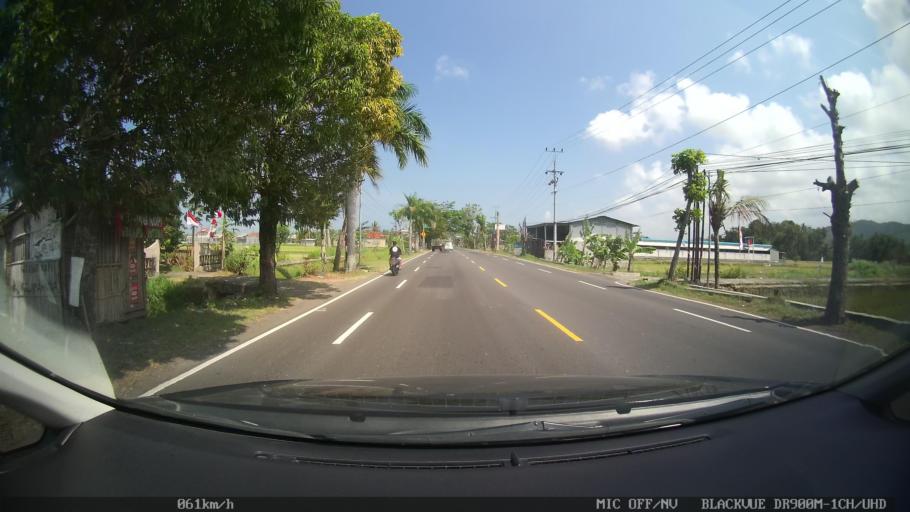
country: ID
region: Daerah Istimewa Yogyakarta
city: Srandakan
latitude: -7.8885
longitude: 110.0953
